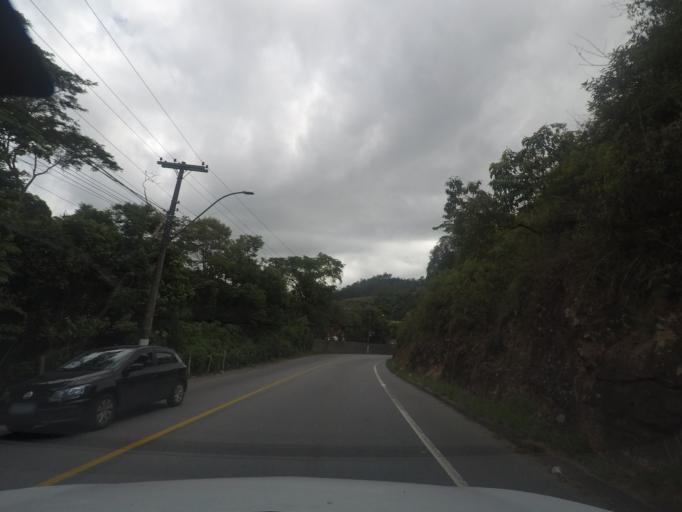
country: BR
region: Rio de Janeiro
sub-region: Teresopolis
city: Teresopolis
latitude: -22.3884
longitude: -42.9574
